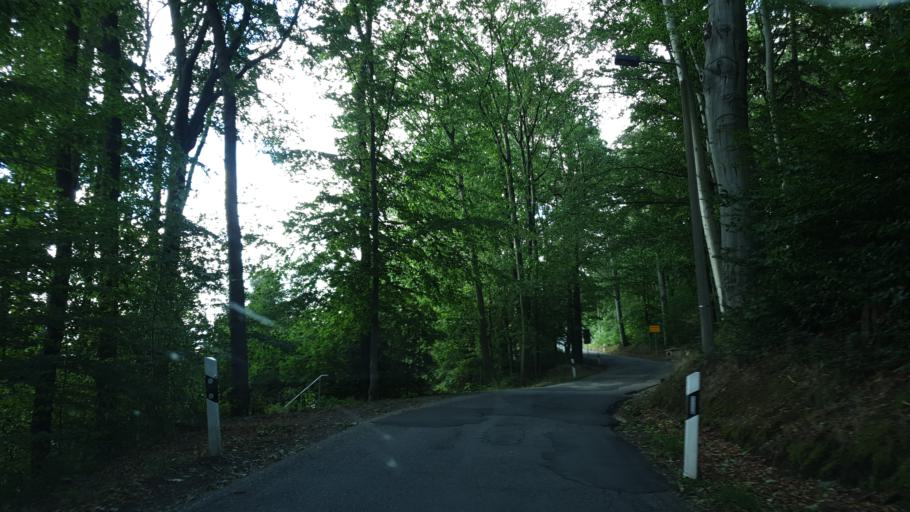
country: DE
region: Saxony
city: Lichtenstein
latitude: 50.7228
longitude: 12.6423
